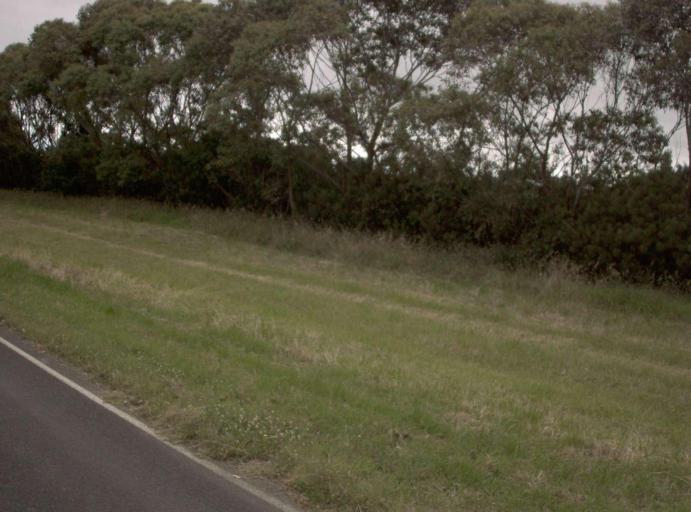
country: AU
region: Victoria
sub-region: Wellington
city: Sale
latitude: -38.5443
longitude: 146.8871
